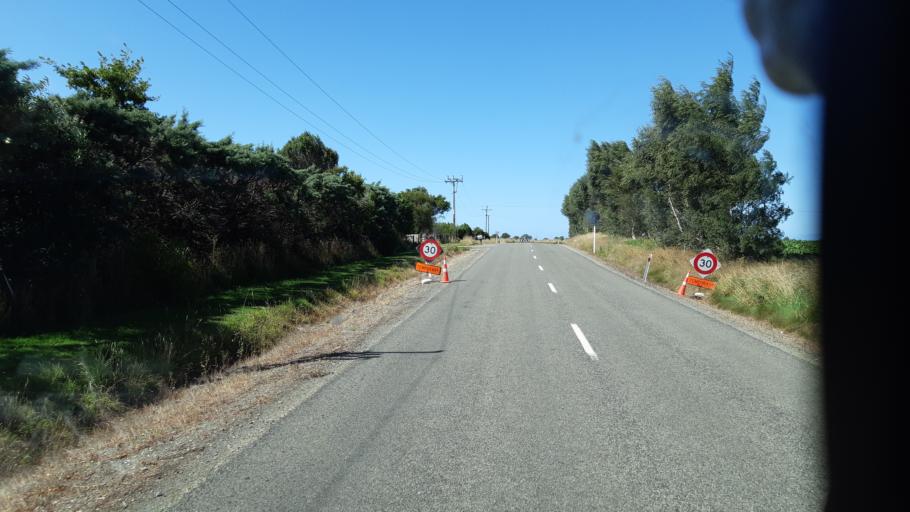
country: NZ
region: Otago
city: Oamaru
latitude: -45.0713
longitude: 170.9605
